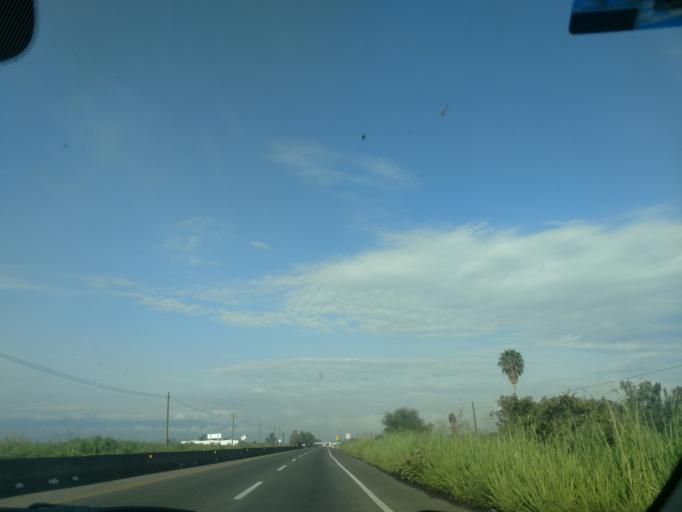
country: MX
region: Jalisco
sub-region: Ameca
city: Los Pocitos
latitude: 20.5351
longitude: -103.9574
